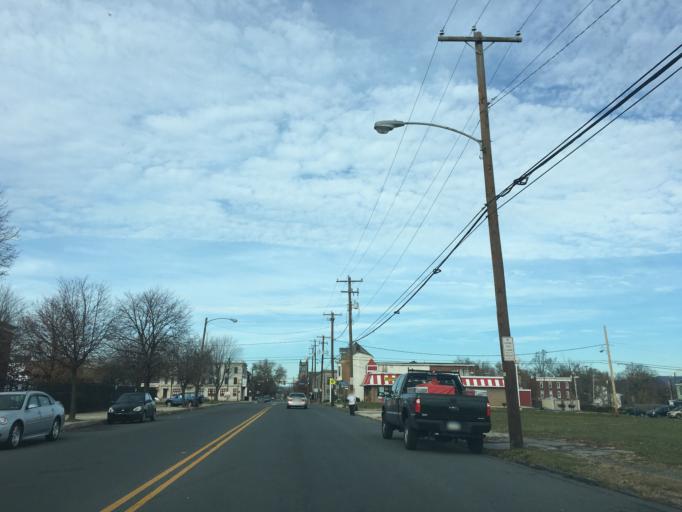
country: US
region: Pennsylvania
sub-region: Dauphin County
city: Harrisburg
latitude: 40.2791
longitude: -76.8896
